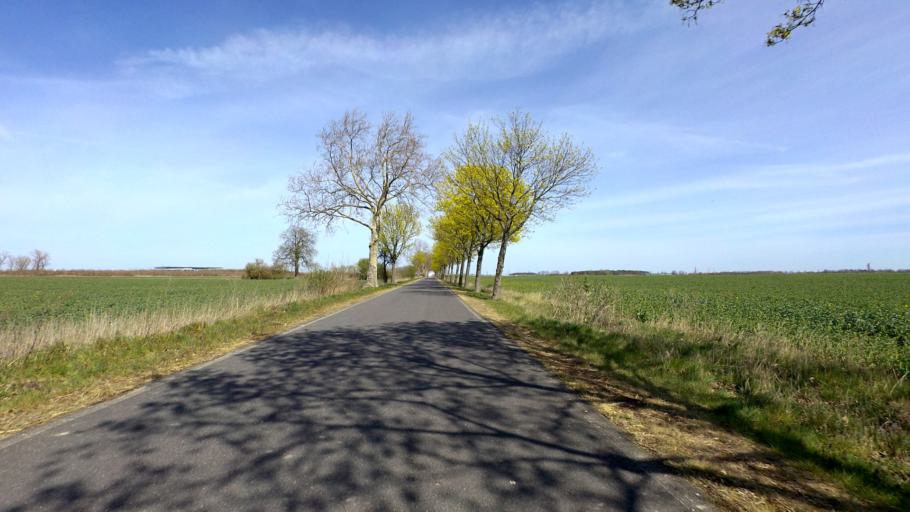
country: DE
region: Brandenburg
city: Schonefeld
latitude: 52.3461
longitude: 13.5116
